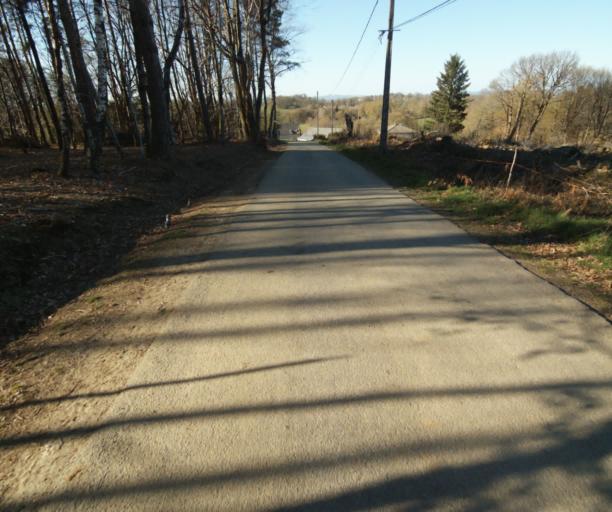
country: FR
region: Limousin
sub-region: Departement de la Correze
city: Seilhac
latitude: 45.3926
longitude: 1.7060
